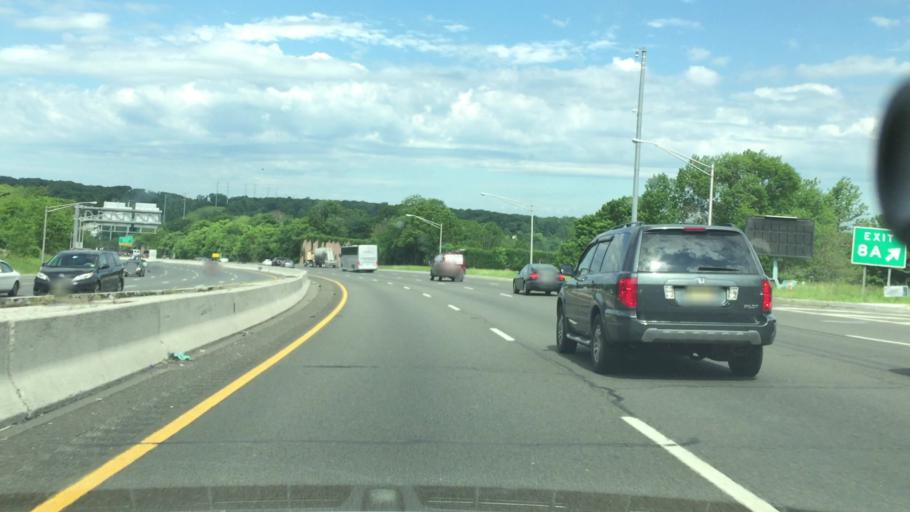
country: US
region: New Jersey
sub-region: Essex County
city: West Orange
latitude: 40.7943
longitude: -74.2500
